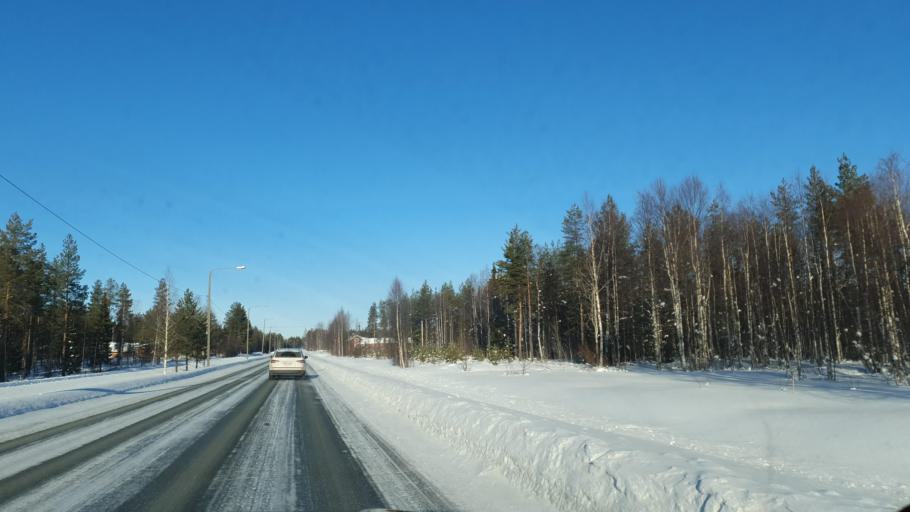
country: FI
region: Lapland
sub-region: Torniolaakso
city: Pello
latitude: 66.7441
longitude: 23.9178
